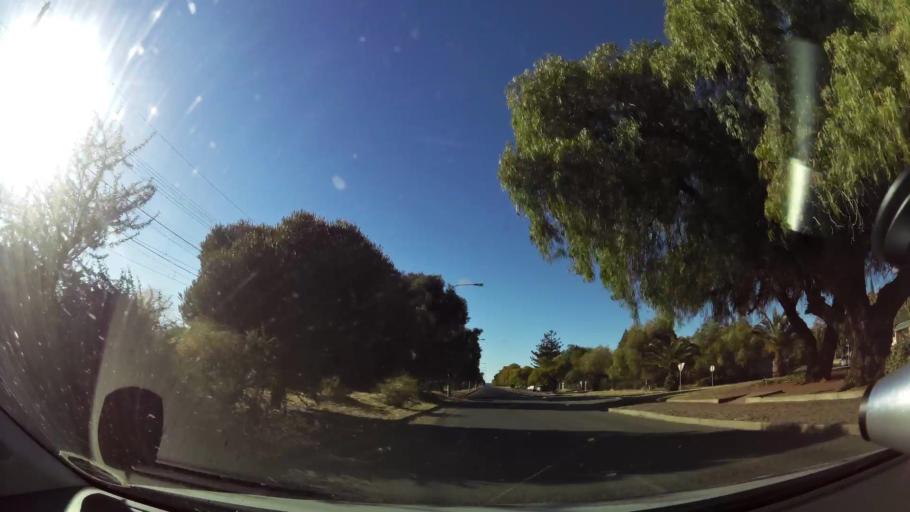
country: ZA
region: Northern Cape
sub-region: Frances Baard District Municipality
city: Kimberley
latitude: -28.7428
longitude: 24.7788
